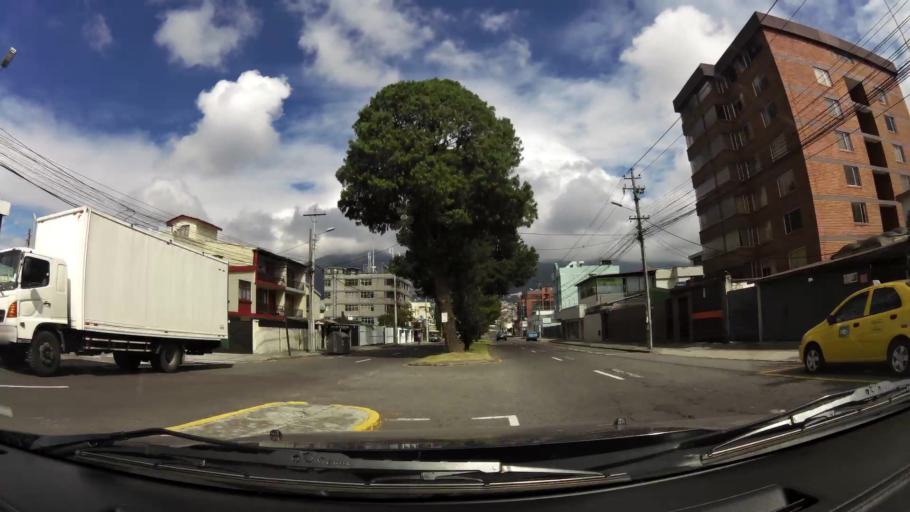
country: EC
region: Pichincha
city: Quito
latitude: -0.1530
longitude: -78.4815
